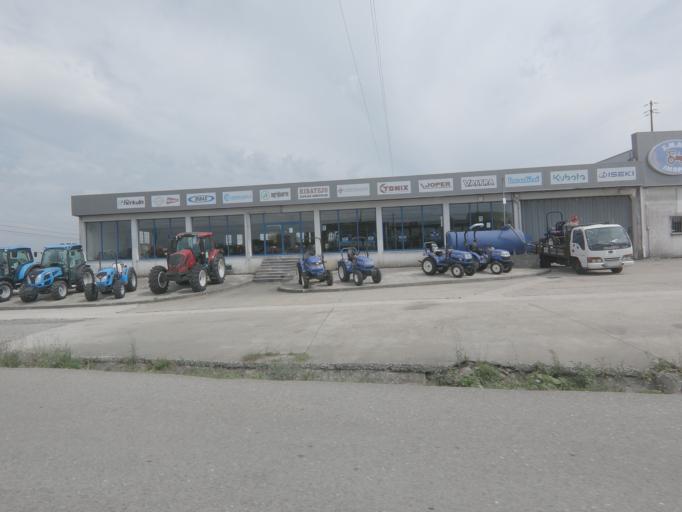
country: PT
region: Leiria
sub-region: Pombal
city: Pombal
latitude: 39.8740
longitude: -8.6876
